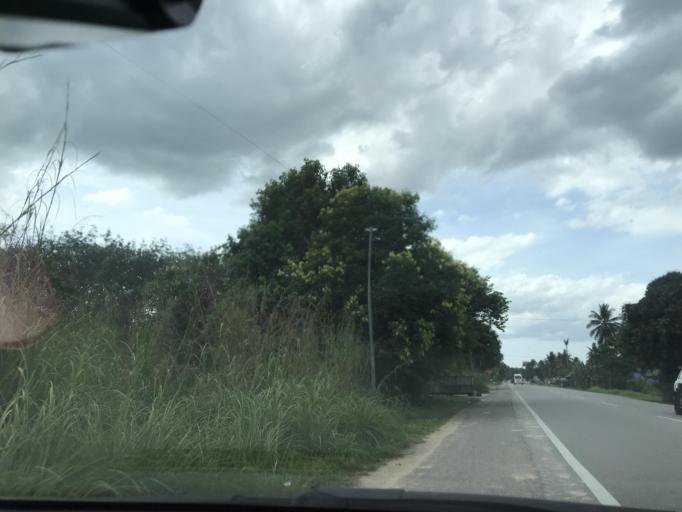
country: MY
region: Kelantan
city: Kampong Pangkal Kalong
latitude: 5.9520
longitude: 102.1926
